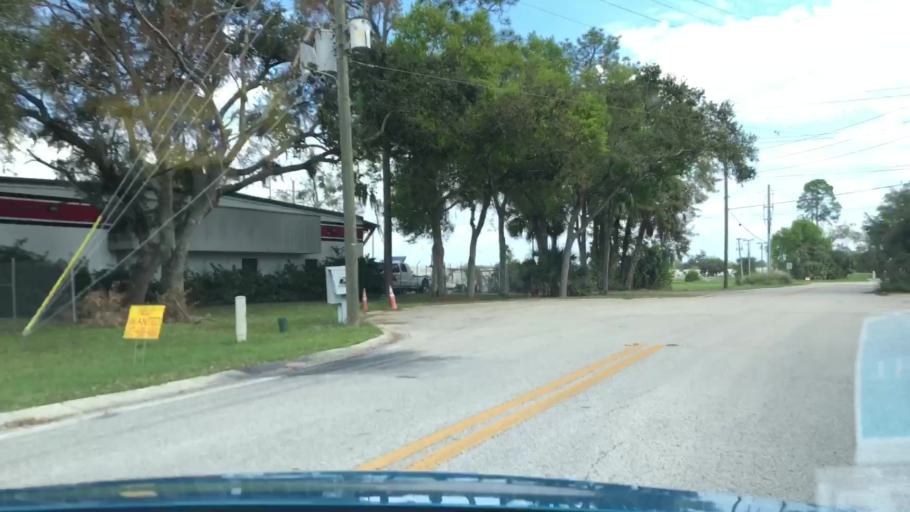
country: US
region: Florida
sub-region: Seminole County
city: Sanford
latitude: 28.8208
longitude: -81.3312
